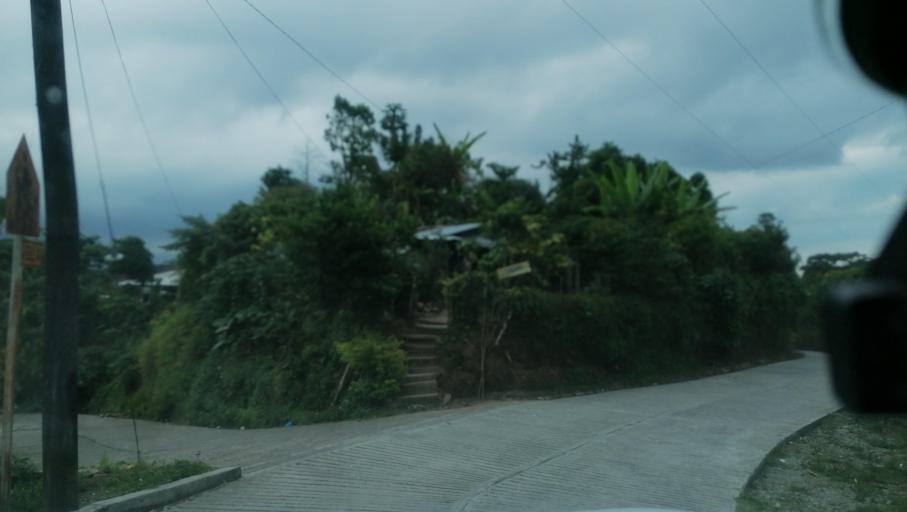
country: MX
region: Chiapas
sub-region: Cacahoatan
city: Benito Juarez
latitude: 15.0786
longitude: -92.1621
